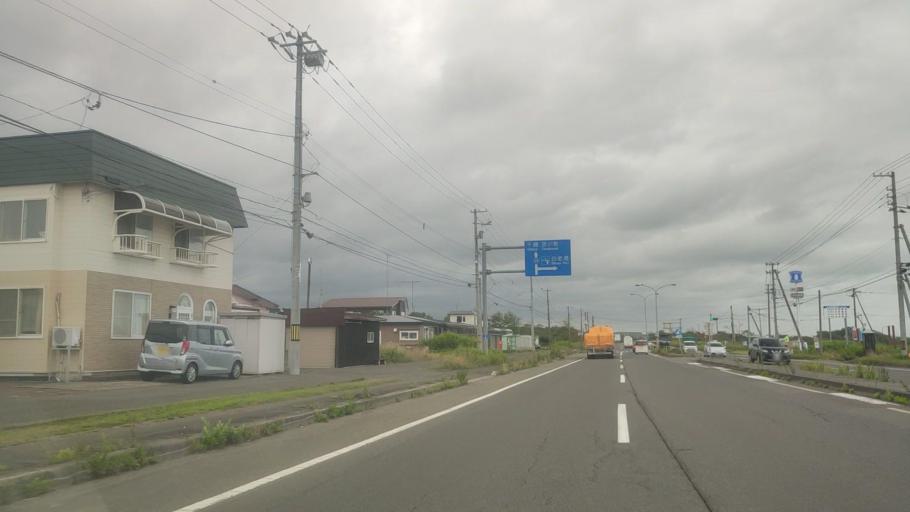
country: JP
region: Hokkaido
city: Shiraoi
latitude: 42.5284
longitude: 141.3211
